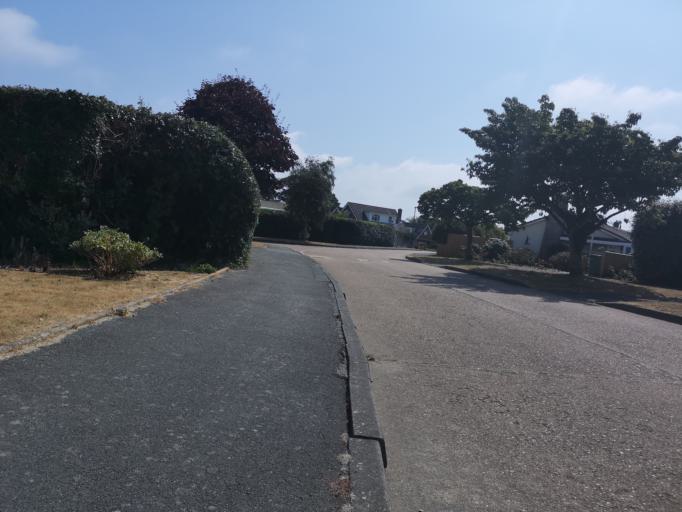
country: GB
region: England
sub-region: Isle of Wight
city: Bembridge
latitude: 50.6858
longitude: -1.0914
